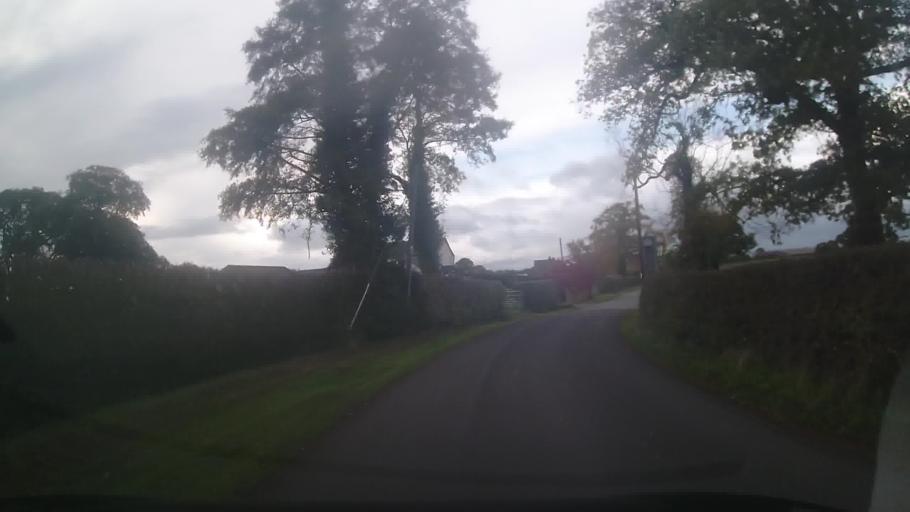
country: GB
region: England
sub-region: Shropshire
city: Wem
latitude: 52.9110
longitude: -2.7386
